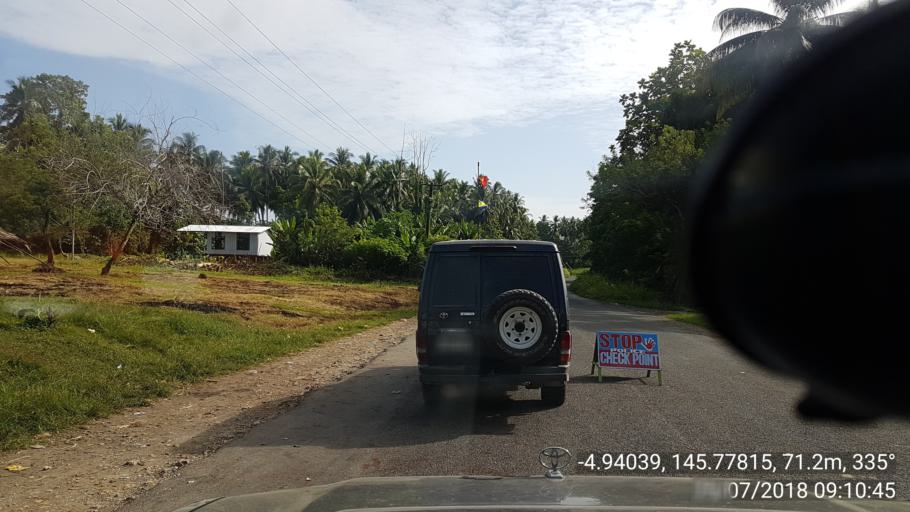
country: PG
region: Madang
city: Madang
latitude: -4.9404
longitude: 145.7781
